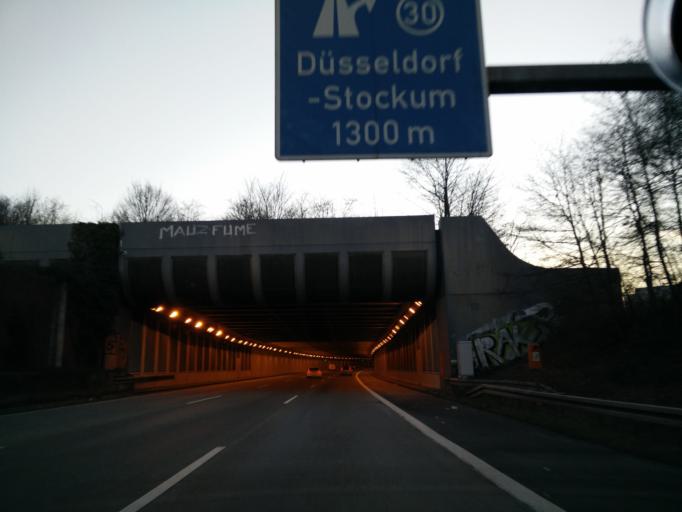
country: DE
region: North Rhine-Westphalia
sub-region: Regierungsbezirk Dusseldorf
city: Dusseldorf
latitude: 51.2766
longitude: 6.7749
